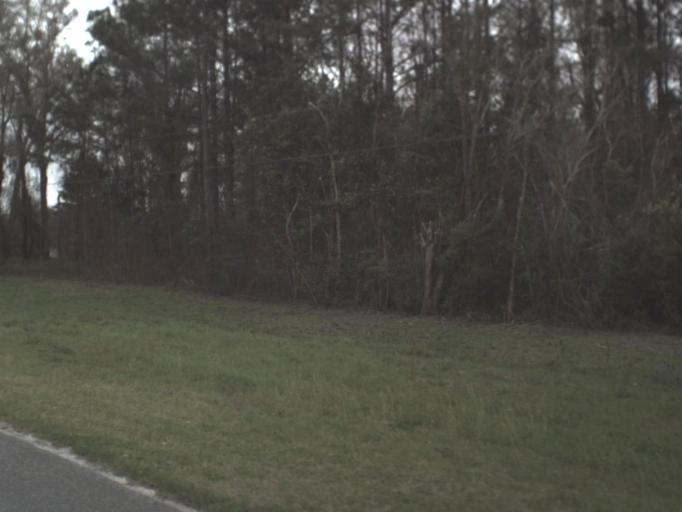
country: US
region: Florida
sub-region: Wakulla County
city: Crawfordville
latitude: 30.1128
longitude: -84.3750
